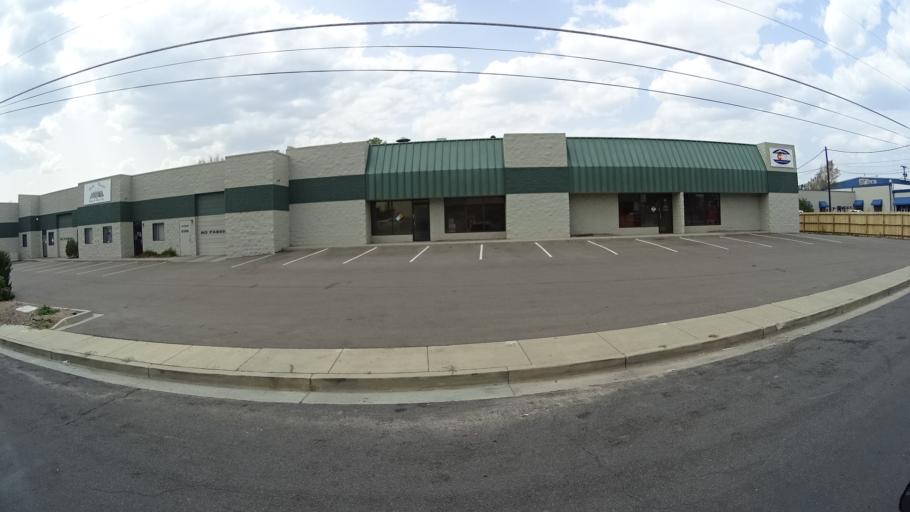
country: US
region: Colorado
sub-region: El Paso County
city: Colorado Springs
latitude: 38.8380
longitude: -104.7630
